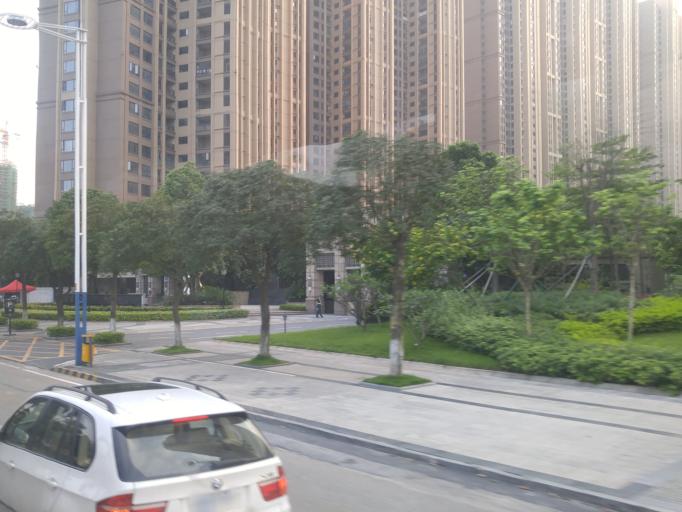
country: CN
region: Guangdong
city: Foshan
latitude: 23.0674
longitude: 113.1405
